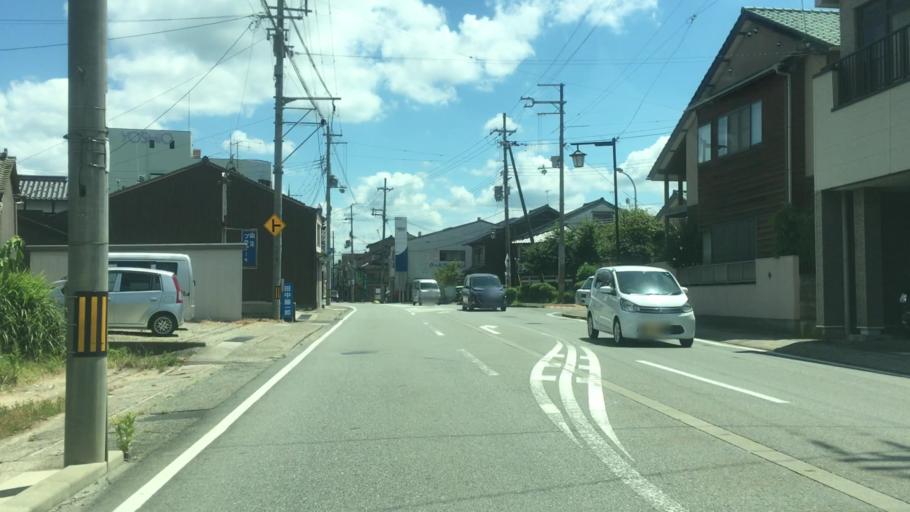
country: JP
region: Hyogo
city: Toyooka
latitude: 35.5394
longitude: 134.8243
